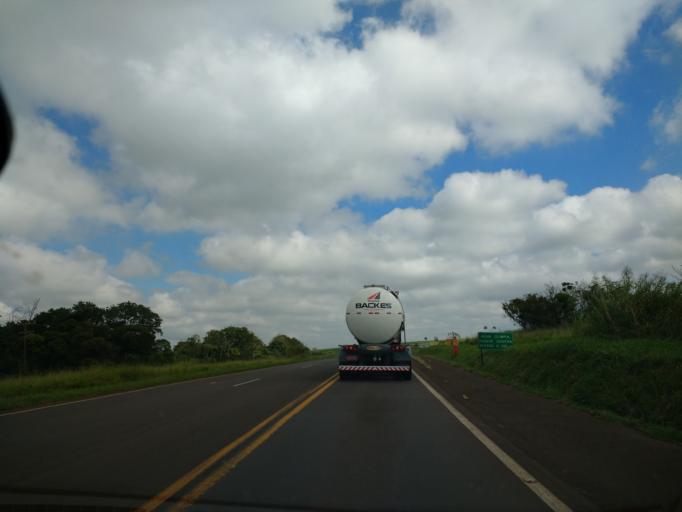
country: BR
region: Parana
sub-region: Cruzeiro Do Oeste
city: Cruzeiro do Oeste
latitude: -23.7723
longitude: -53.0162
